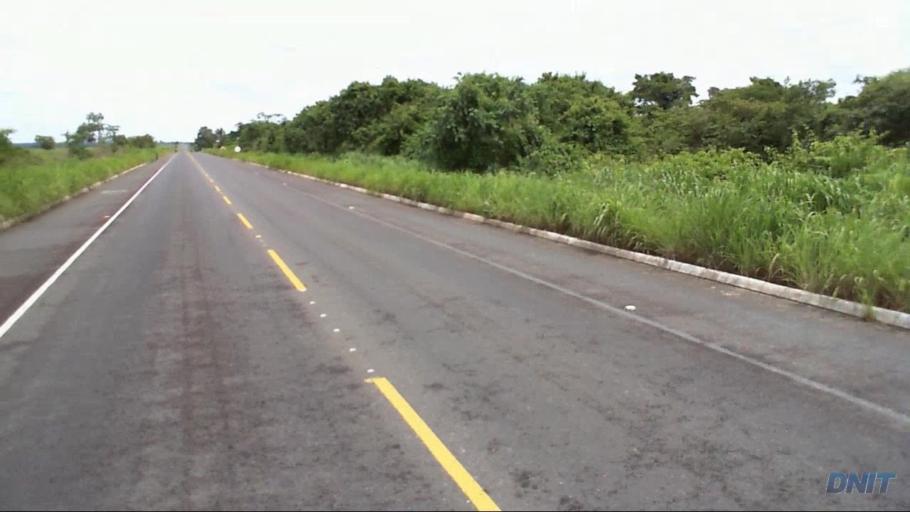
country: BR
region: Goias
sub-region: Sao Miguel Do Araguaia
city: Sao Miguel do Araguaia
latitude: -13.2948
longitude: -50.2325
